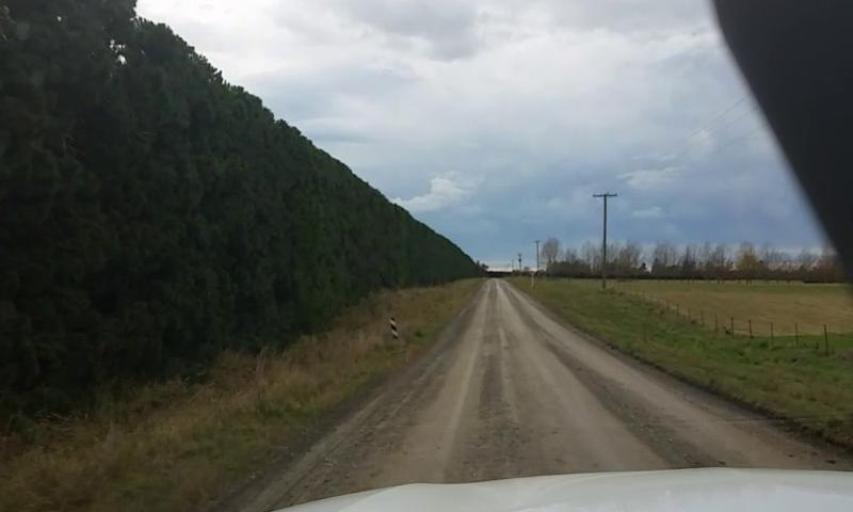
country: NZ
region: Canterbury
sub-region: Waimakariri District
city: Kaiapoi
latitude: -43.2910
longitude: 172.4379
